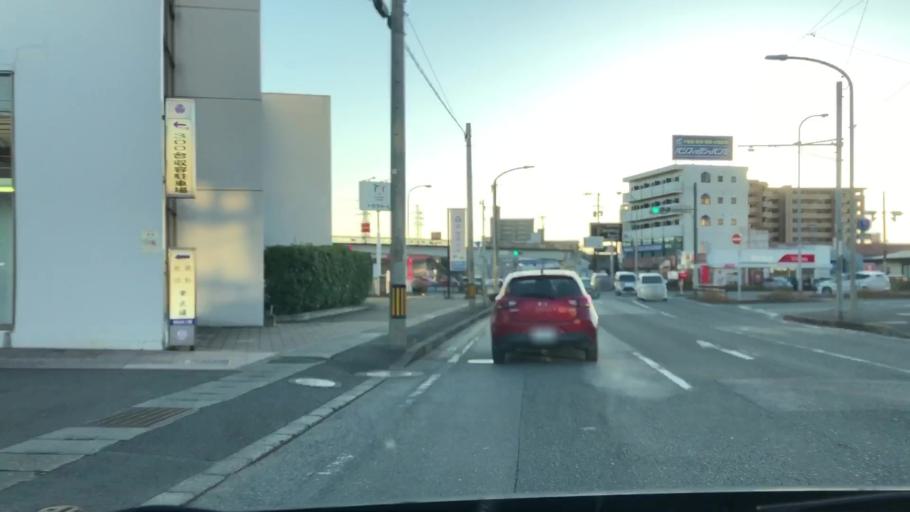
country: JP
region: Fukuoka
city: Fukuoka-shi
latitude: 33.6255
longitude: 130.4403
